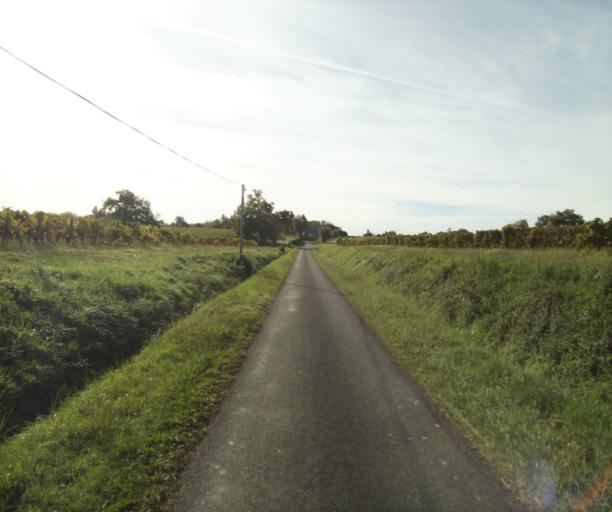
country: FR
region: Midi-Pyrenees
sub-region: Departement du Gers
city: Eauze
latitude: 43.8889
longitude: 0.1329
